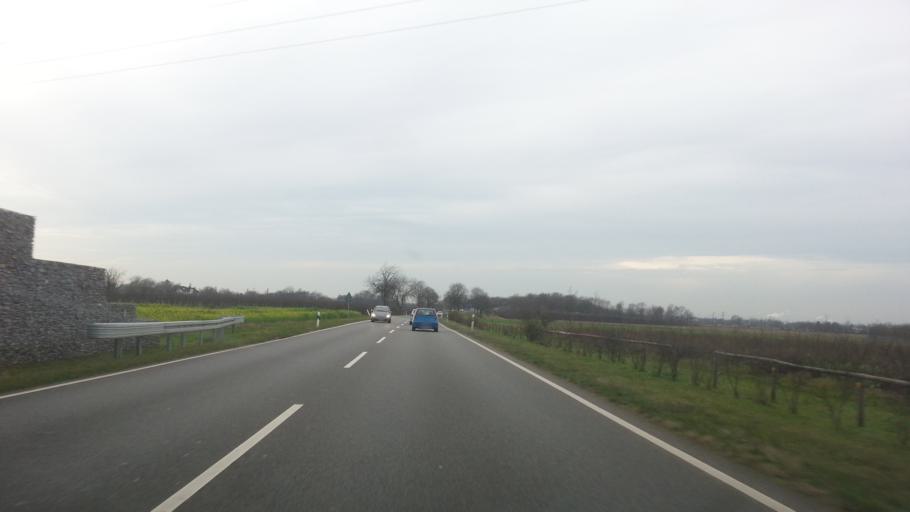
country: DE
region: Baden-Wuerttemberg
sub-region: Karlsruhe Region
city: Schriesheim
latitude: 49.4799
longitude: 8.6506
